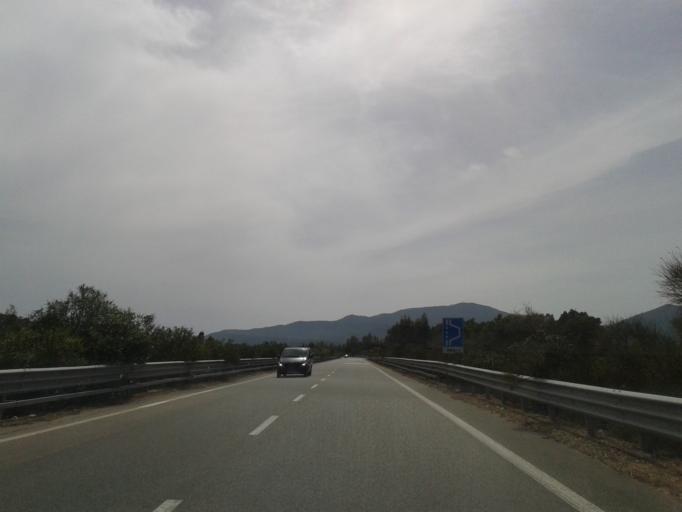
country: IT
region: Sardinia
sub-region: Provincia di Cagliari
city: Olia Speciosa
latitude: 39.2574
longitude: 9.5321
